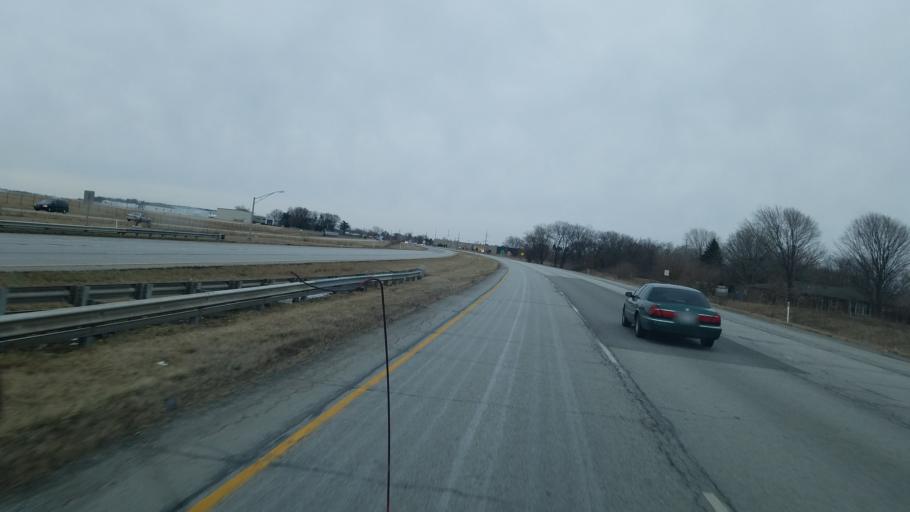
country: US
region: Indiana
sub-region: Porter County
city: Valparaiso
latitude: 41.4514
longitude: -87.0234
